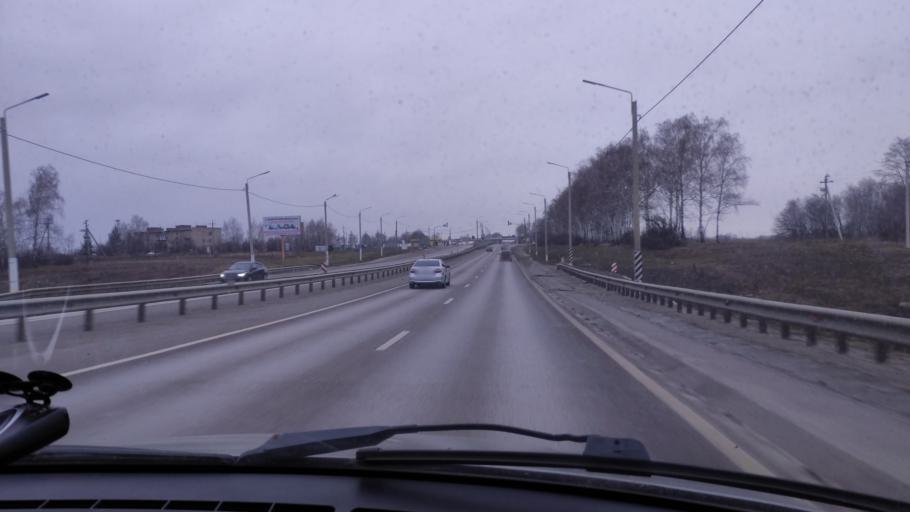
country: RU
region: Tambov
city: Komsomolets
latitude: 52.7322
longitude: 41.3054
